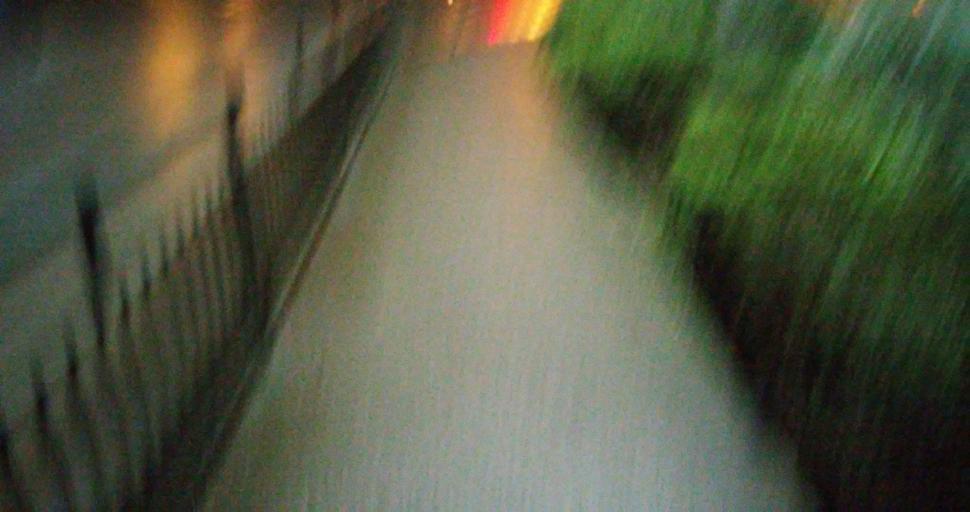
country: CL
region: Los Rios
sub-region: Provincia de Valdivia
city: Valdivia
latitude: -39.8119
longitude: -73.2470
